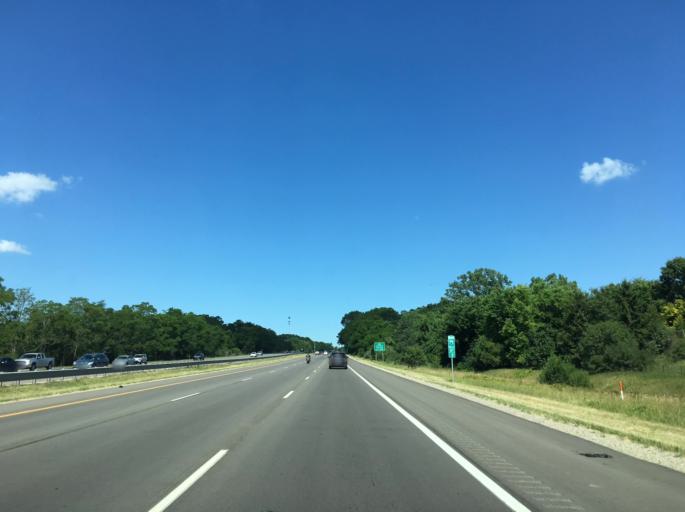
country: US
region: Michigan
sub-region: Oakland County
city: Clarkston
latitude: 42.7289
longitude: -83.3640
